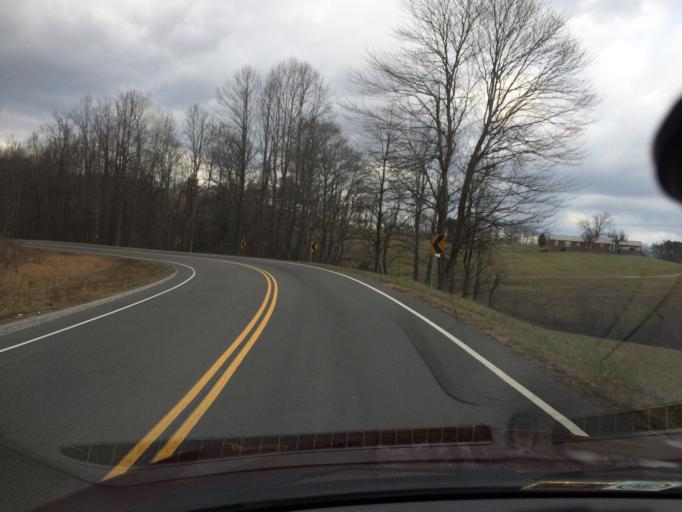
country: US
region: Virginia
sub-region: Patrick County
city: Stuart
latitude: 36.7211
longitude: -80.2393
